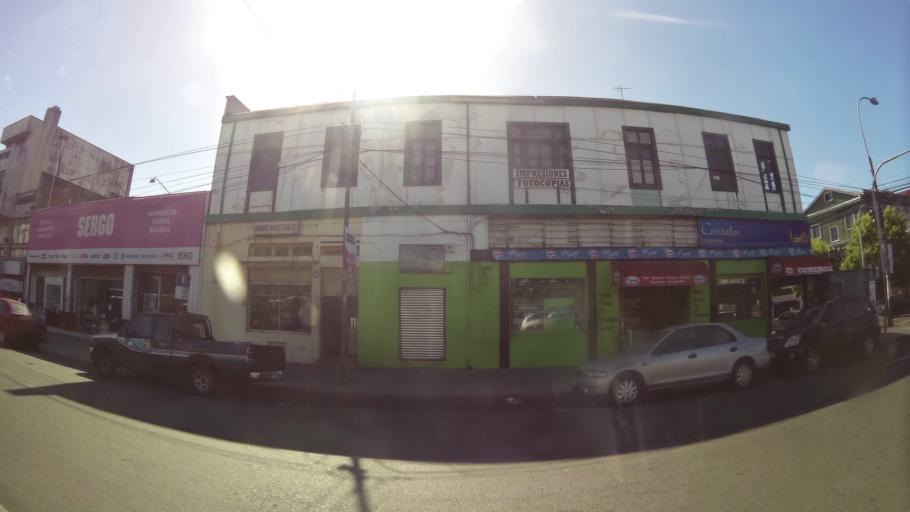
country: CL
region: Valparaiso
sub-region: Provincia de Valparaiso
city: Valparaiso
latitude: -33.0470
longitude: -71.6125
